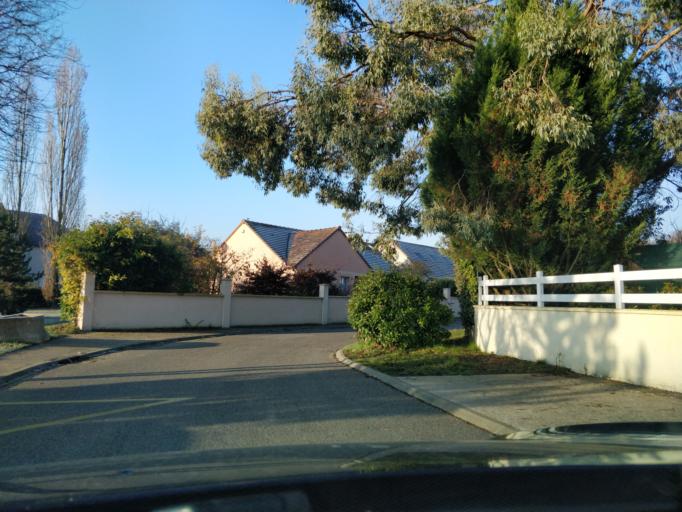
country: FR
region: Ile-de-France
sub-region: Departement de l'Essonne
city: Forges-les-Bains
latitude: 48.6299
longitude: 2.1008
